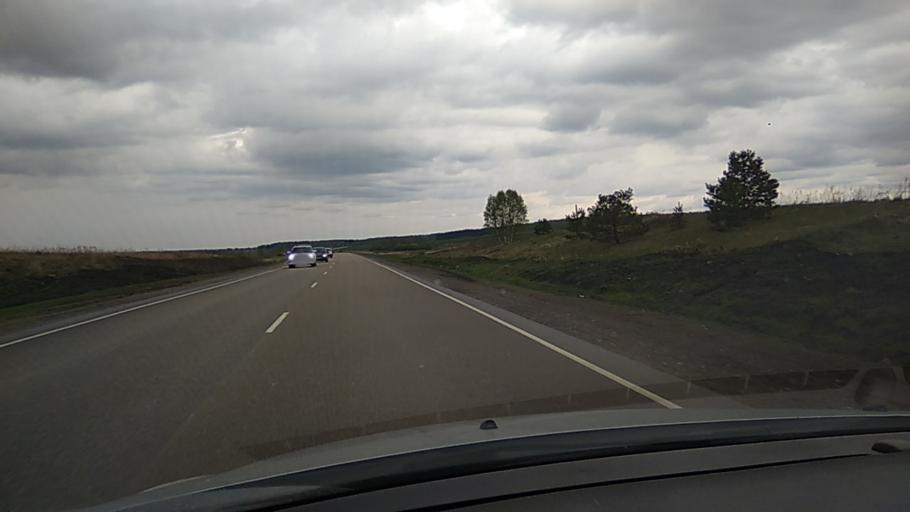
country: RU
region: Kurgan
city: Kataysk
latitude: 56.2976
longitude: 62.4277
